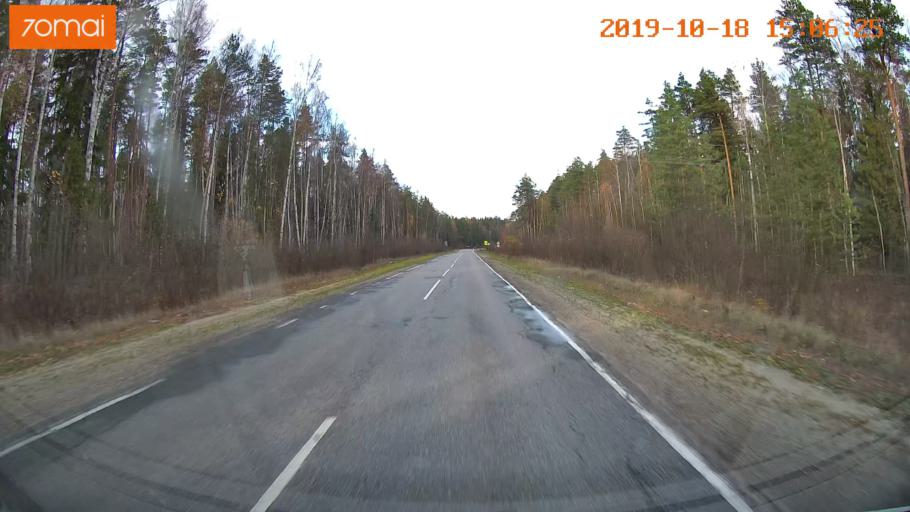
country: RU
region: Vladimir
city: Gus'-Khrustal'nyy
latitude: 55.5299
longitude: 40.5785
